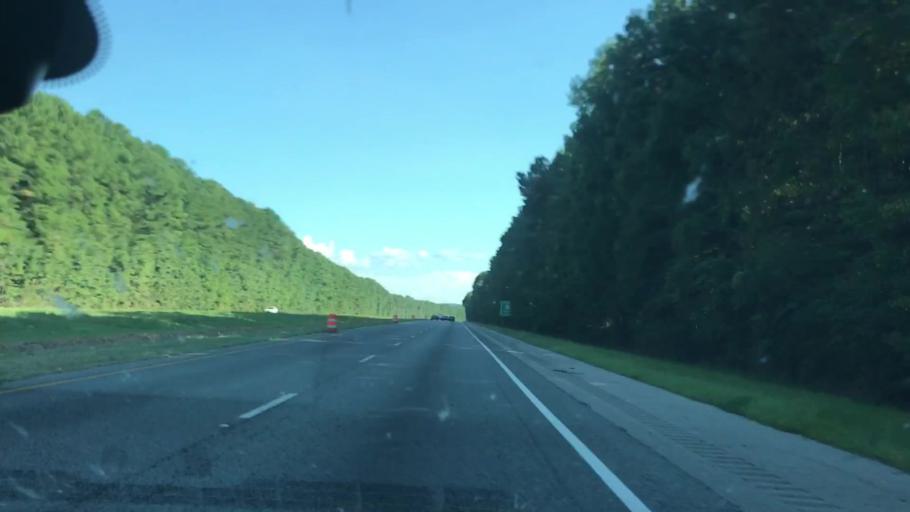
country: US
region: Georgia
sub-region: Harris County
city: Hamilton
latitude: 32.7673
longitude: -85.0198
